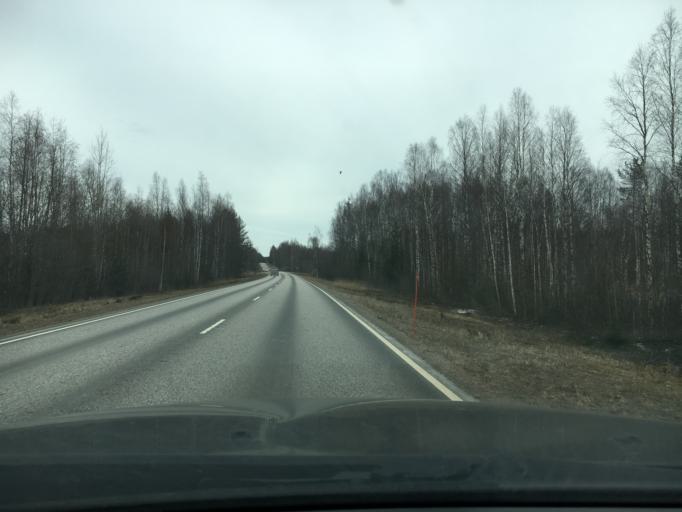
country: FI
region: Central Finland
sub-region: AEaenekoski
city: Sumiainen
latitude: 62.5711
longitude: 26.0725
